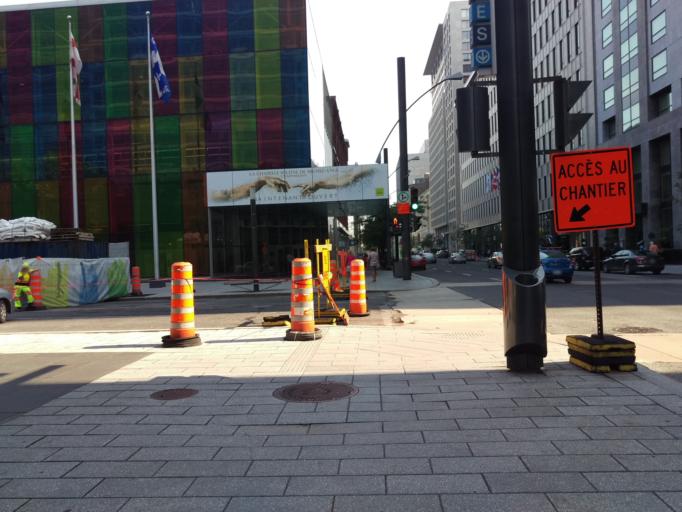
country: CA
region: Quebec
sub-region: Montreal
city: Montreal
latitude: 45.5030
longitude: -73.5606
